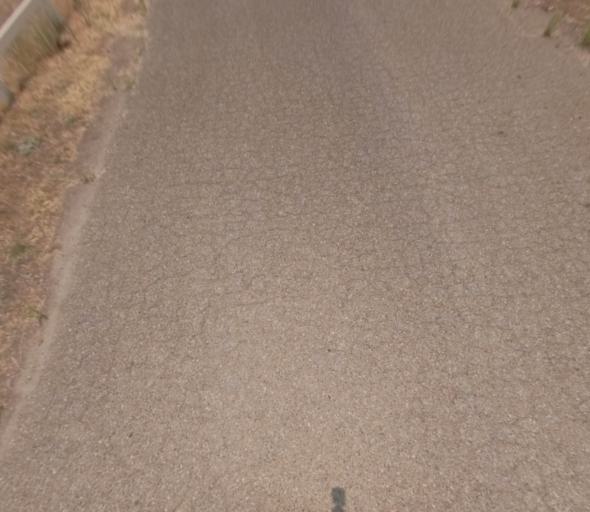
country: US
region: California
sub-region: Madera County
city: Oakhurst
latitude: 37.2651
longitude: -119.5849
